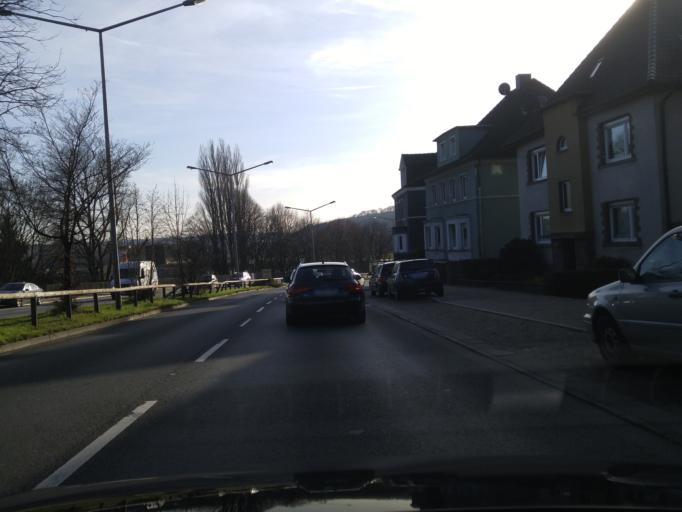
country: DE
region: North Rhine-Westphalia
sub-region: Regierungsbezirk Dusseldorf
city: Essen
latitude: 51.4305
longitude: 7.0553
